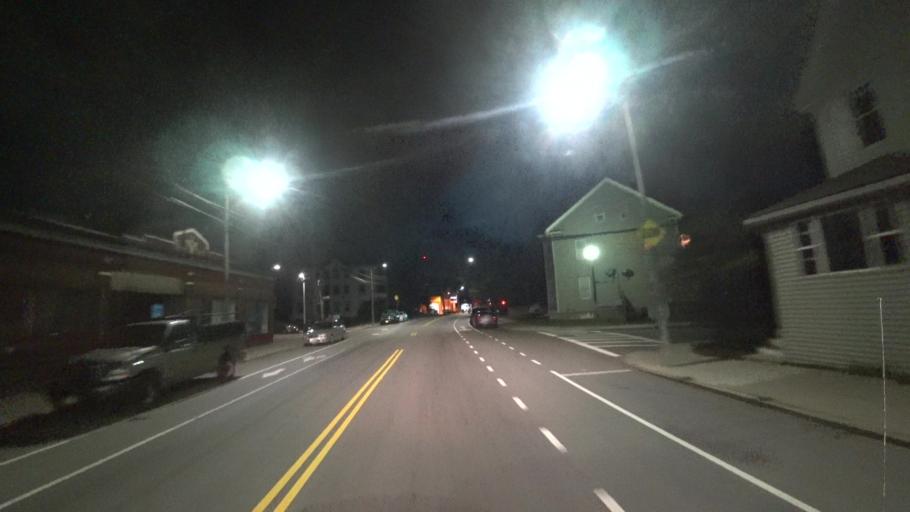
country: US
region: Massachusetts
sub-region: Middlesex County
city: Cambridge
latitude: 42.3610
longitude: -71.1296
